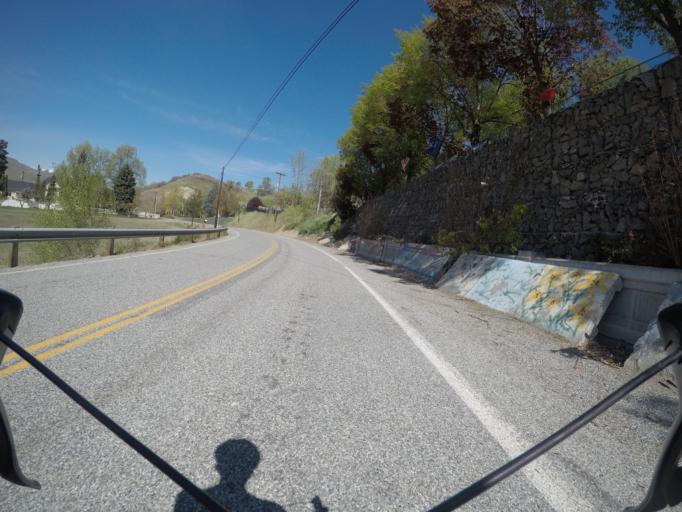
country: US
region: Washington
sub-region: Chelan County
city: Sunnyslope
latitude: 47.4689
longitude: -120.3467
